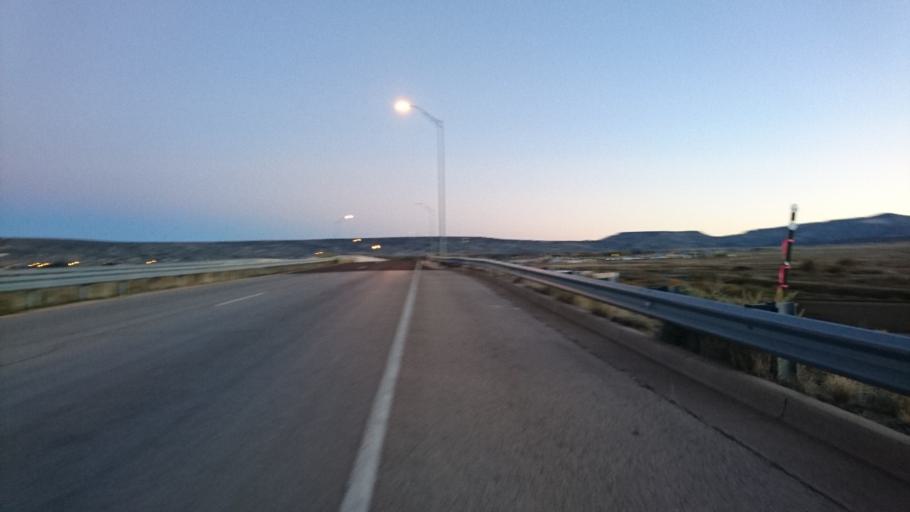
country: US
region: New Mexico
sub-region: Cibola County
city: Grants
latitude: 35.1363
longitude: -107.8278
